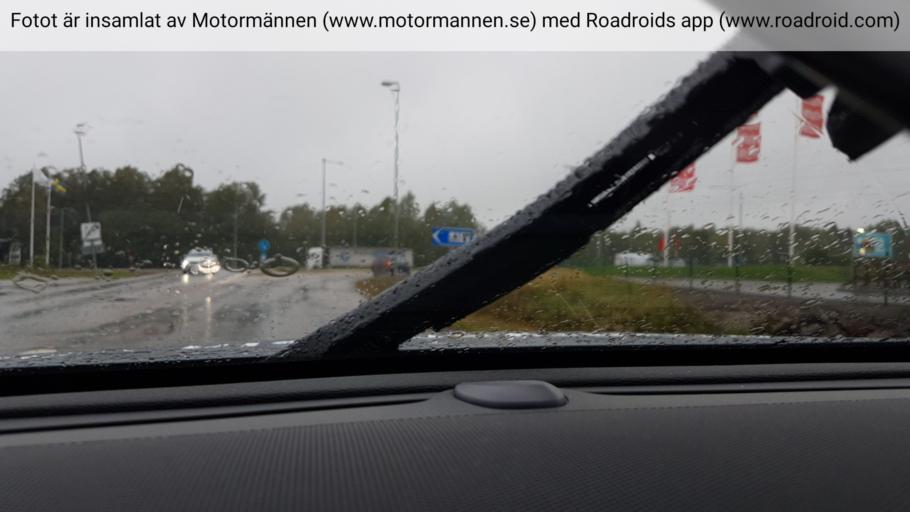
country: SE
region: Vaestra Goetaland
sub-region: Amals Kommun
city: Amal
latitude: 59.0556
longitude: 12.6769
